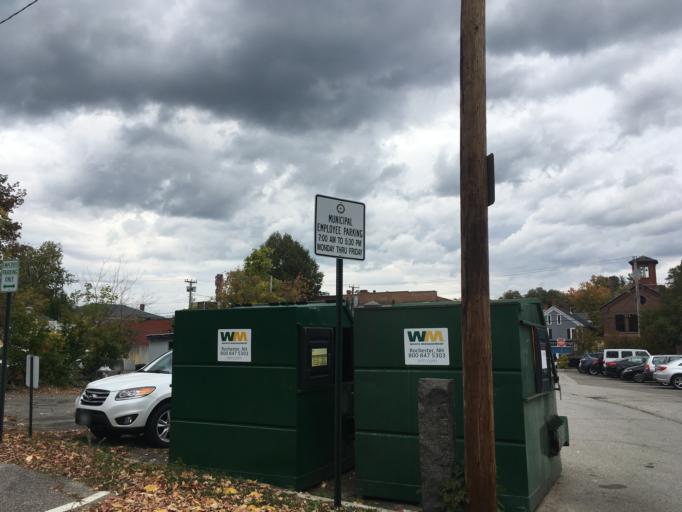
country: US
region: New Hampshire
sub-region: Rockingham County
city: Exeter
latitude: 42.9805
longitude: -70.9457
